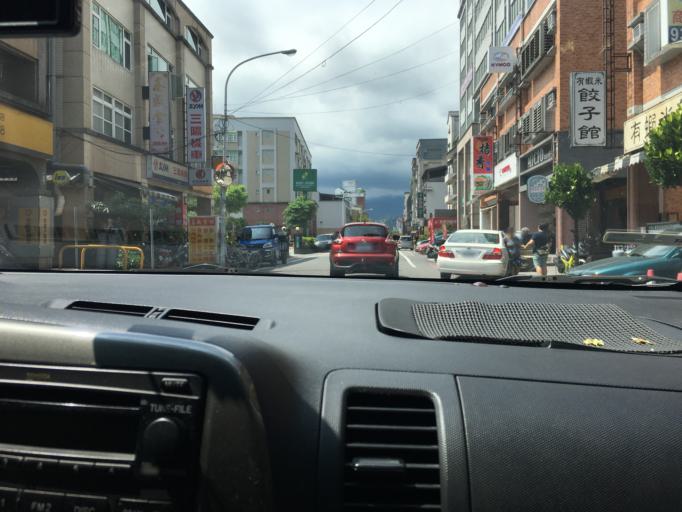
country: TW
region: Taiwan
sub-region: Yilan
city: Yilan
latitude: 24.7460
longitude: 121.7409
